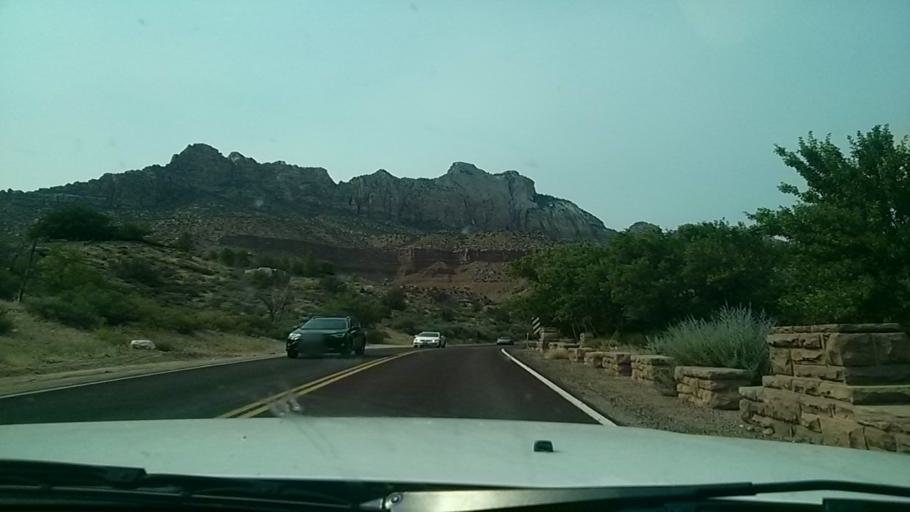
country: US
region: Utah
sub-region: Washington County
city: Hildale
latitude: 37.1688
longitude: -113.0132
